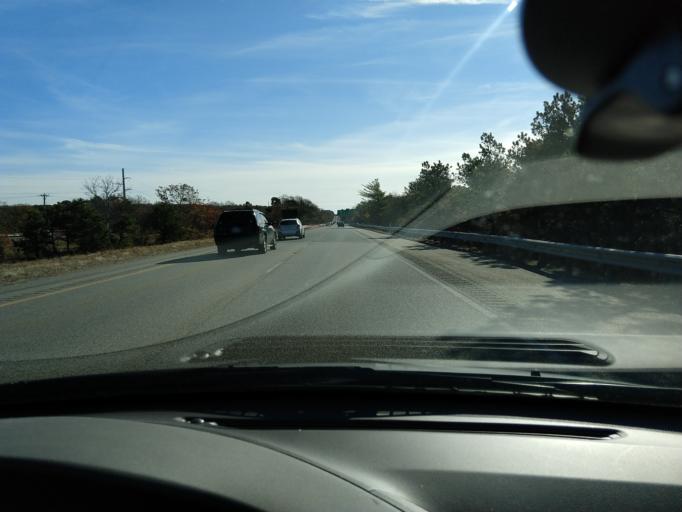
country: US
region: Massachusetts
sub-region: Barnstable County
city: Sagamore
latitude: 41.8149
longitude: -70.5547
